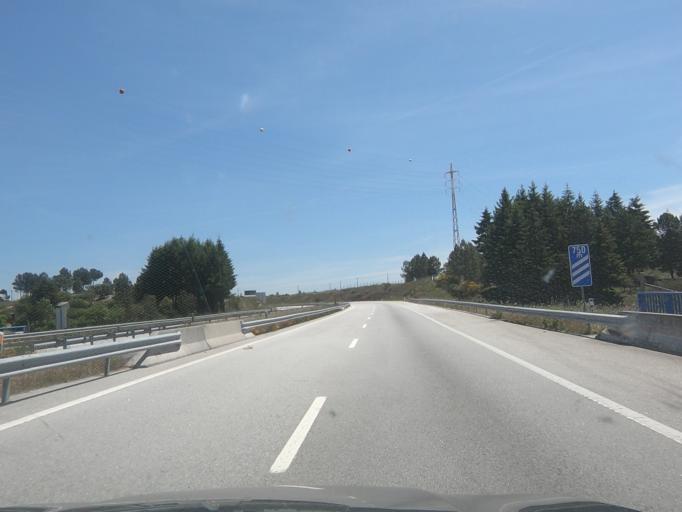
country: PT
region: Guarda
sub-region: Guarda
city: Sequeira
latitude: 40.5620
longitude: -7.2290
